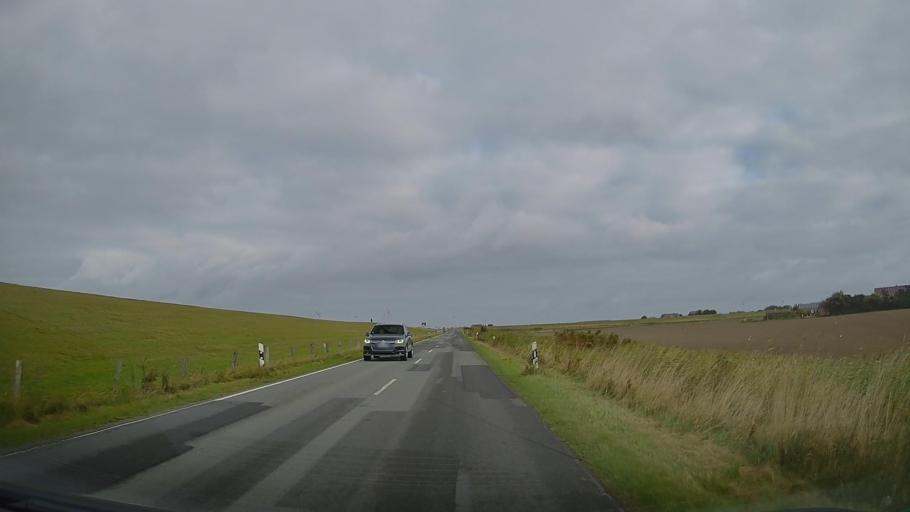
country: DE
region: Schleswig-Holstein
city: Galmsbull
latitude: 54.6991
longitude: 8.7539
